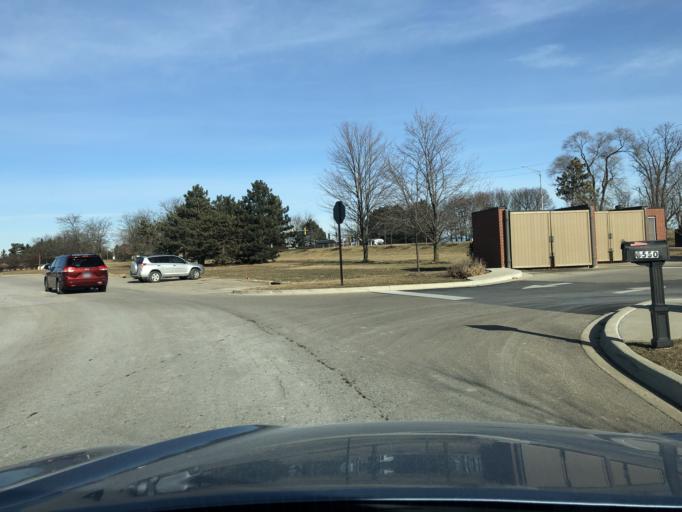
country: US
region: Illinois
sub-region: Lake County
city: Grandwood Park
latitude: 42.3864
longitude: -87.9641
